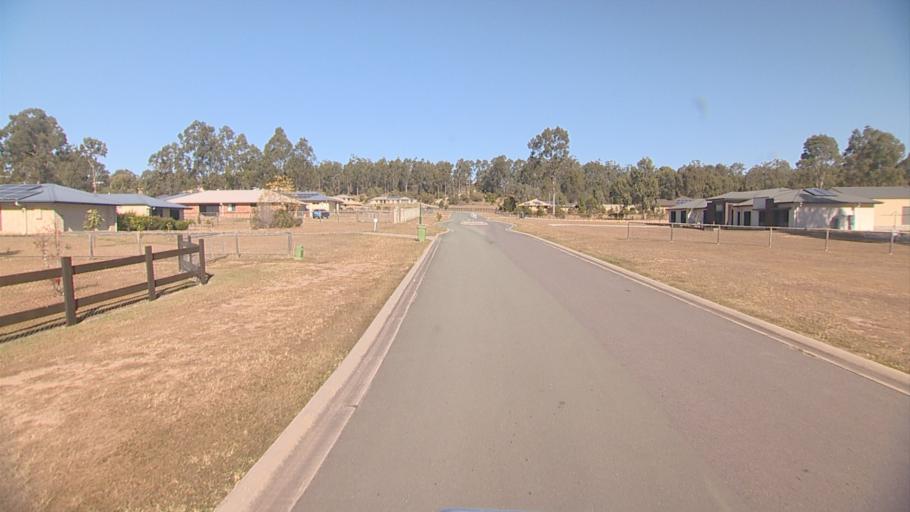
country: AU
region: Queensland
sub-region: Logan
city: Cedar Vale
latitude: -27.8660
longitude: 153.0318
